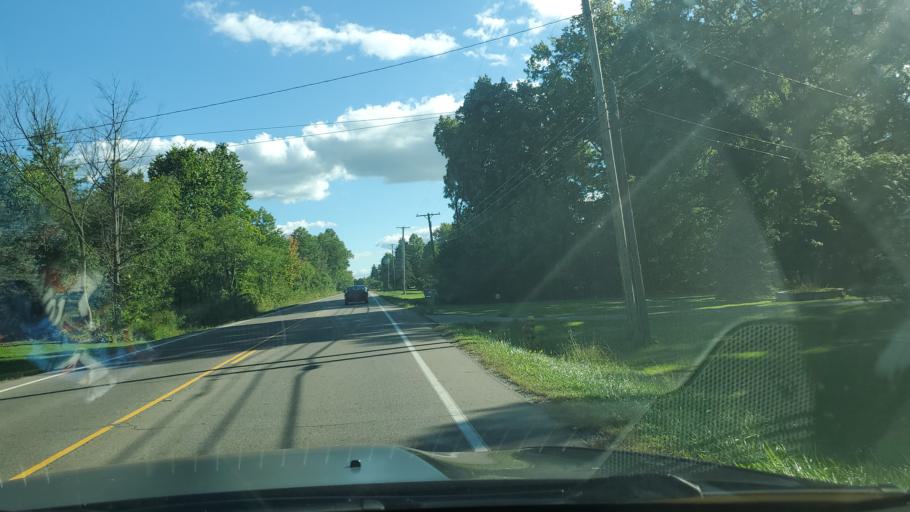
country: US
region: Ohio
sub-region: Mahoning County
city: Austintown
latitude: 41.0769
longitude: -80.7625
